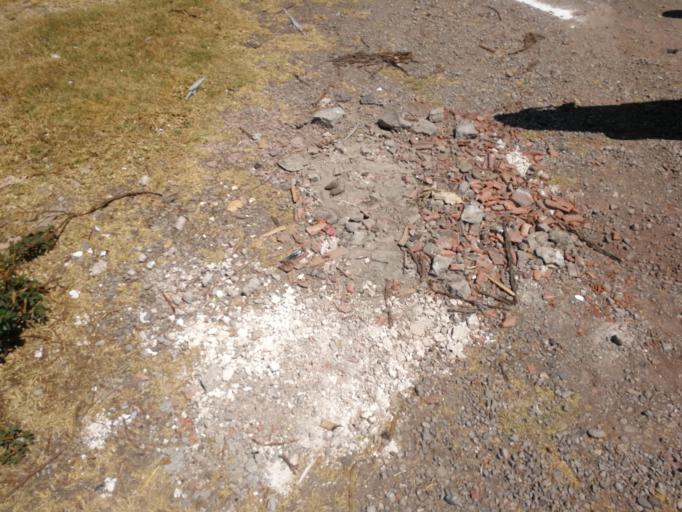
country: PE
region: Cusco
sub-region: Provincia de Cusco
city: Cusco
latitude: -13.4956
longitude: -71.9297
